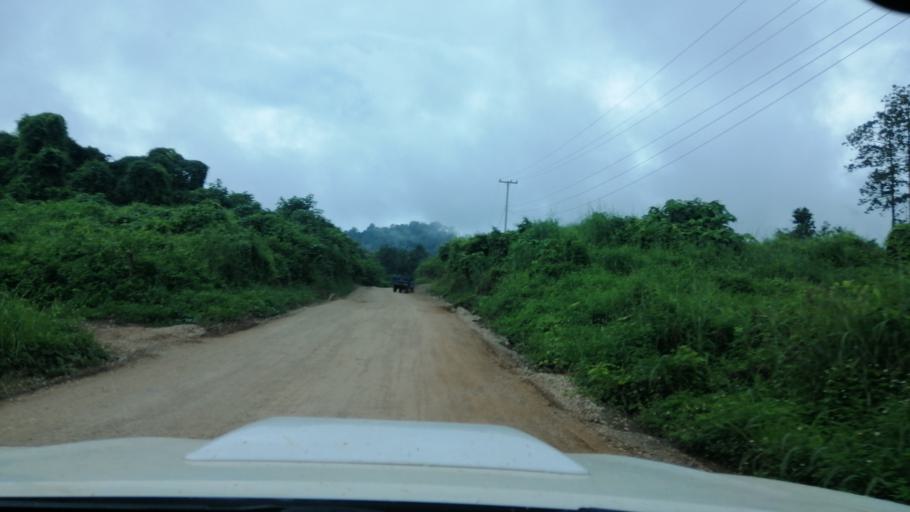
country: LA
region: Xiagnabouli
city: Sainyabuli
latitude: 19.2100
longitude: 101.6981
